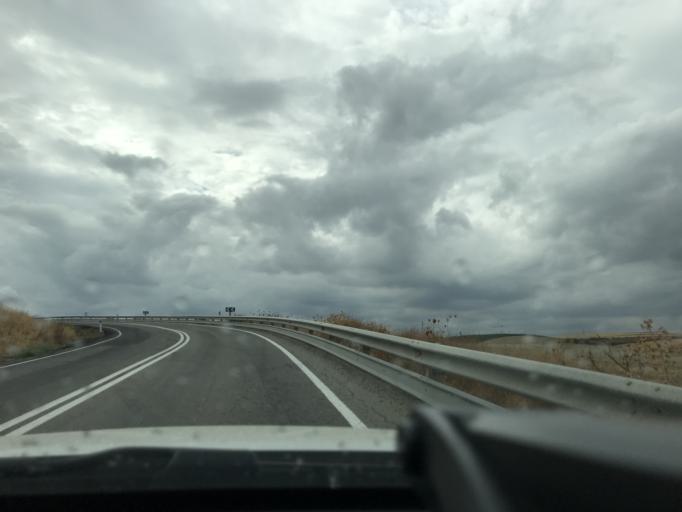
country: ES
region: Andalusia
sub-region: Provincia de Sevilla
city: Cantillana
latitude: 37.6170
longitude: -5.7968
